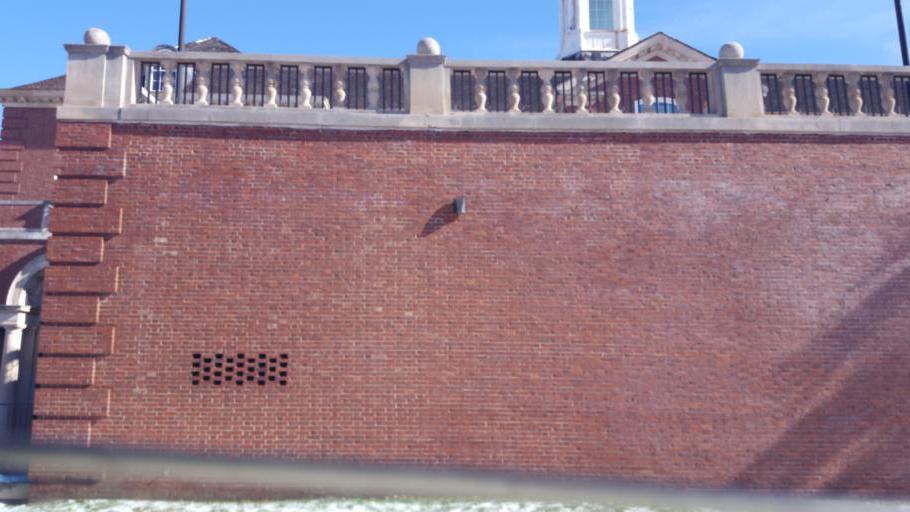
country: US
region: New York
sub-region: Allegany County
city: Wellsville
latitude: 42.1216
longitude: -77.9496
